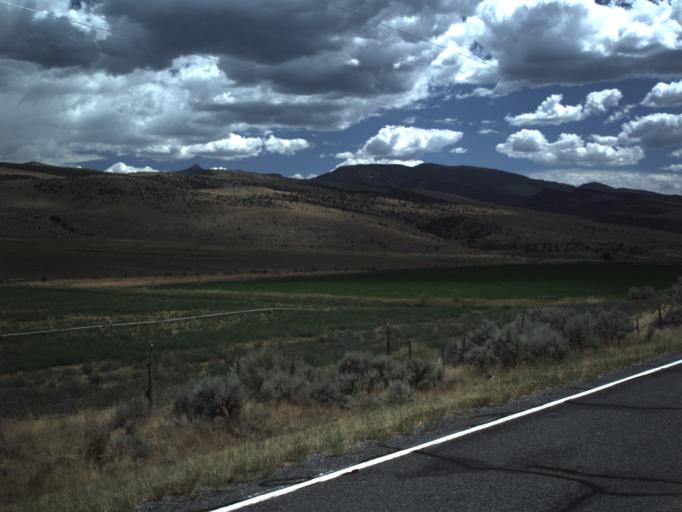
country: US
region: Utah
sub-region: Sanpete County
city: Gunnison
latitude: 39.1514
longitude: -111.7090
